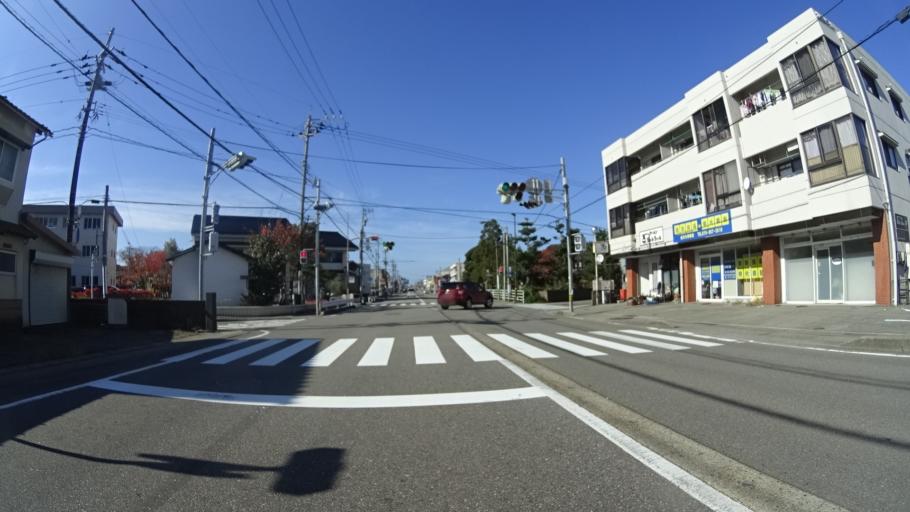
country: JP
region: Ishikawa
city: Kanazawa-shi
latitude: 36.5921
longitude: 136.6108
